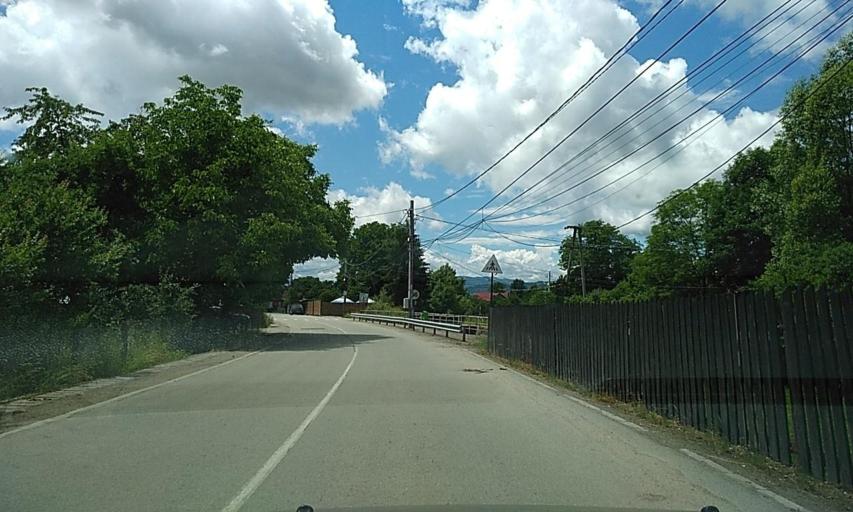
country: RO
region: Hunedoara
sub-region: Oras Petrila
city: Petrila
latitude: 45.4576
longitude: 23.4414
